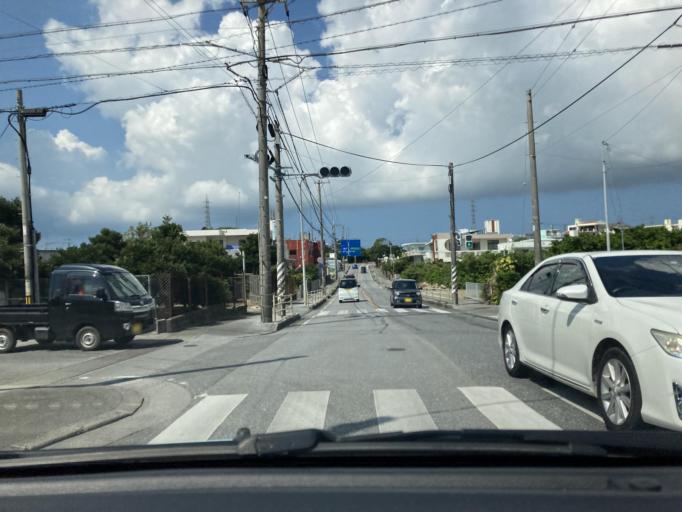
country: JP
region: Okinawa
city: Tomigusuku
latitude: 26.1725
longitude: 127.7315
